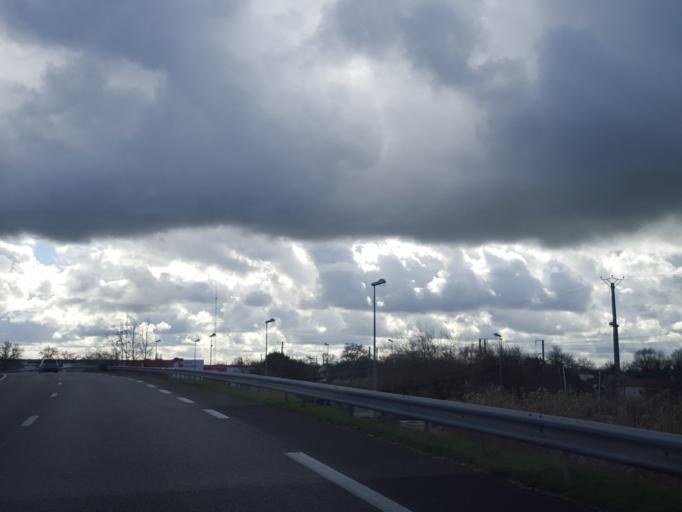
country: FR
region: Pays de la Loire
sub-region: Departement de la Vendee
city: Mouilleron-le-Captif
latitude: 46.7320
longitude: -1.4328
